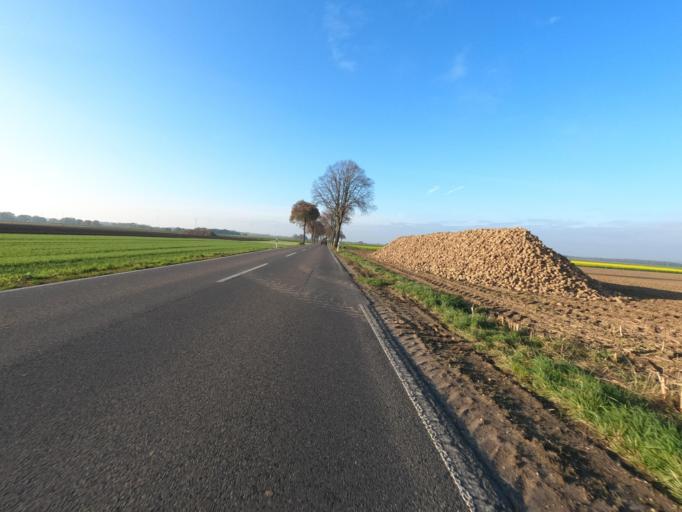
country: DE
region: North Rhine-Westphalia
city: Huckelhoven
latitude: 51.0012
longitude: 6.2020
